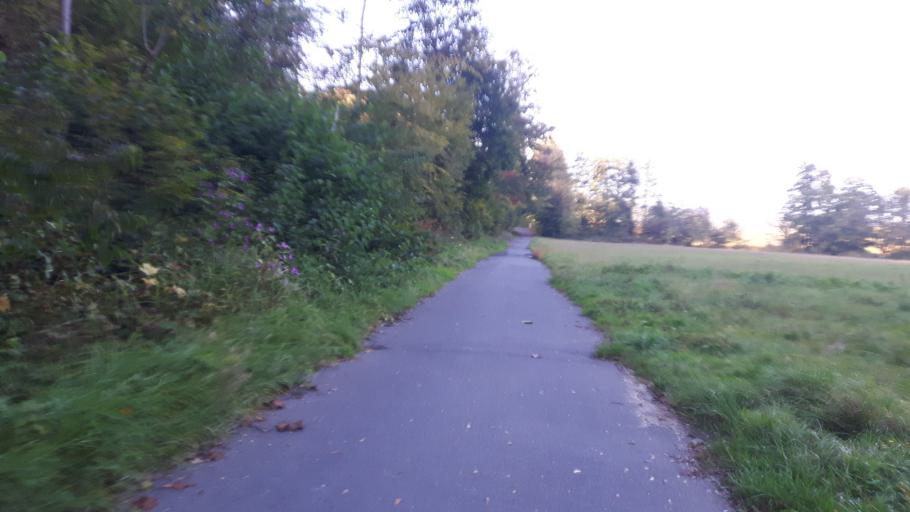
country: DE
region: Rheinland-Pfalz
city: Werkhausen
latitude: 50.7843
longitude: 7.5163
